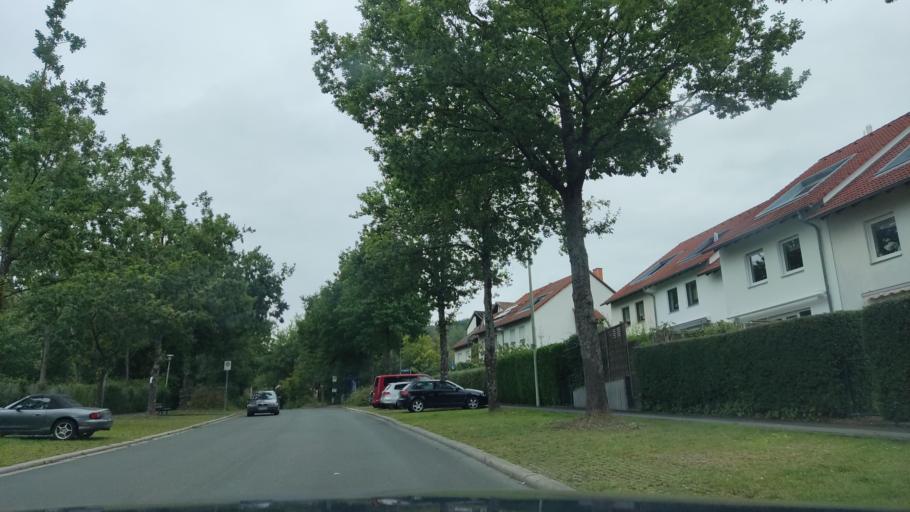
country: DE
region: Bavaria
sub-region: Upper Franconia
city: Kronach
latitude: 50.2368
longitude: 11.3470
